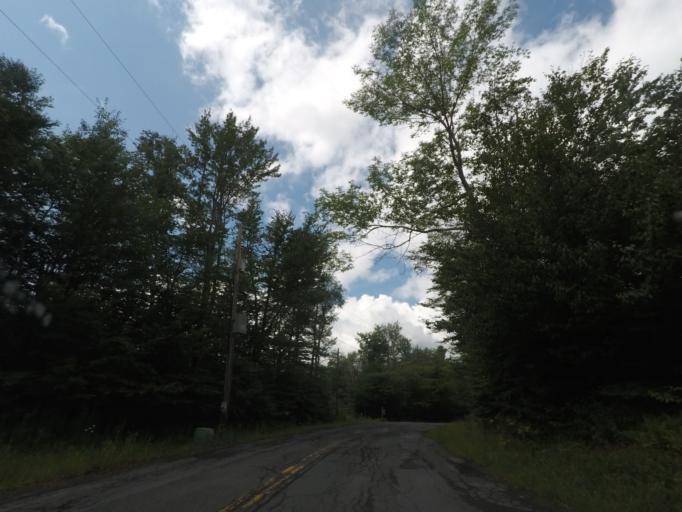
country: US
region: New York
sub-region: Rensselaer County
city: Averill Park
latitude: 42.6546
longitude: -73.4092
